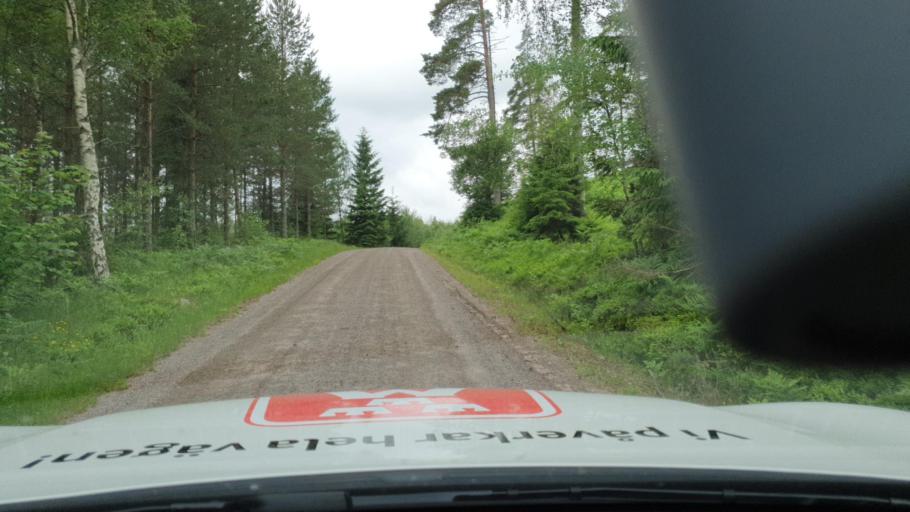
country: SE
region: Vaestra Goetaland
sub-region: Hjo Kommun
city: Hjo
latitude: 58.4073
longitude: 14.3202
